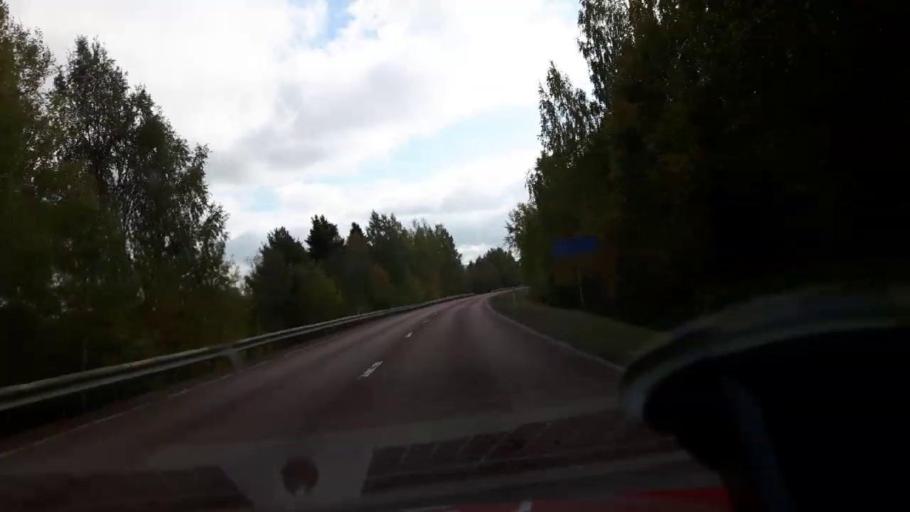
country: SE
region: Gaevleborg
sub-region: Ljusdals Kommun
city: Jaervsoe
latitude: 61.6351
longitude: 16.2671
